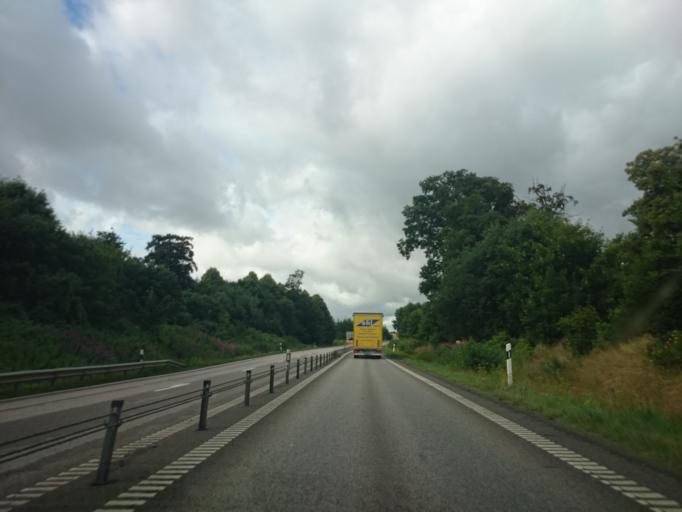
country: SE
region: Skane
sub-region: Horby Kommun
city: Hoerby
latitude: 55.8496
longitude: 13.6034
